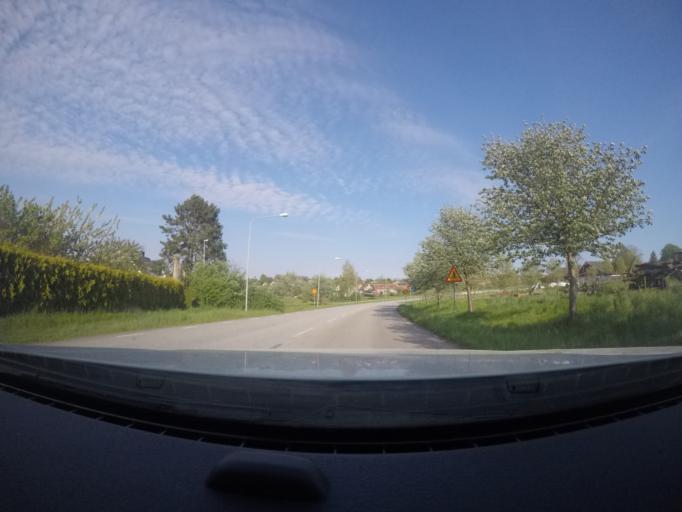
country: SE
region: Skane
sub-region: Helsingborg
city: Glumslov
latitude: 55.9407
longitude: 12.8018
